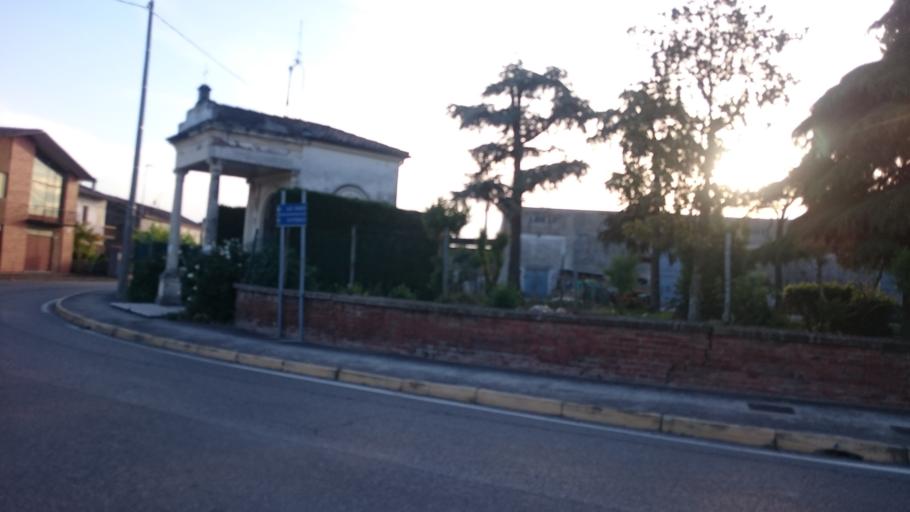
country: IT
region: Veneto
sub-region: Provincia di Verona
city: Casaleone
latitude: 45.1678
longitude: 11.1943
